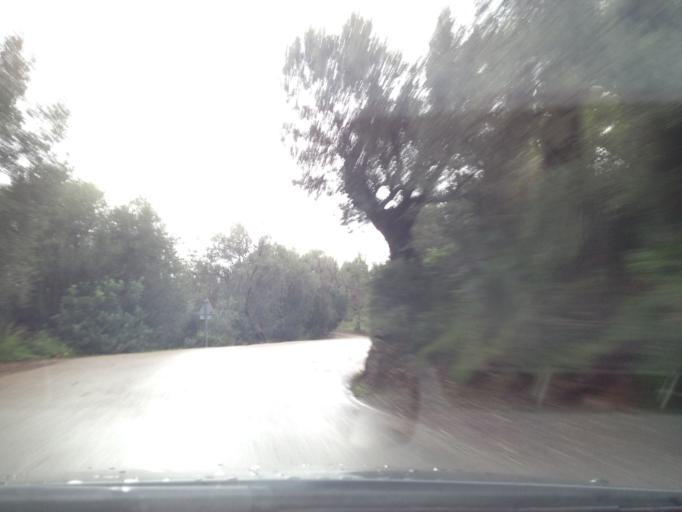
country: ES
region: Balearic Islands
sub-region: Illes Balears
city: Deia
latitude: 39.7739
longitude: 2.6765
